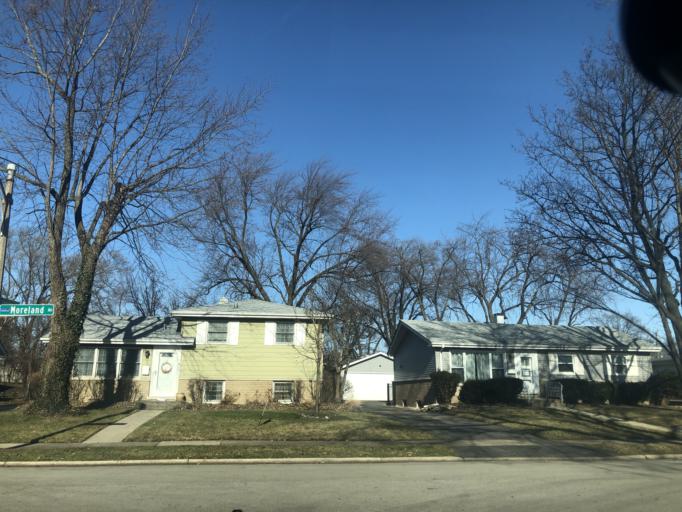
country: US
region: Illinois
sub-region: DuPage County
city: Addison
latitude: 41.9274
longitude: -88.0022
